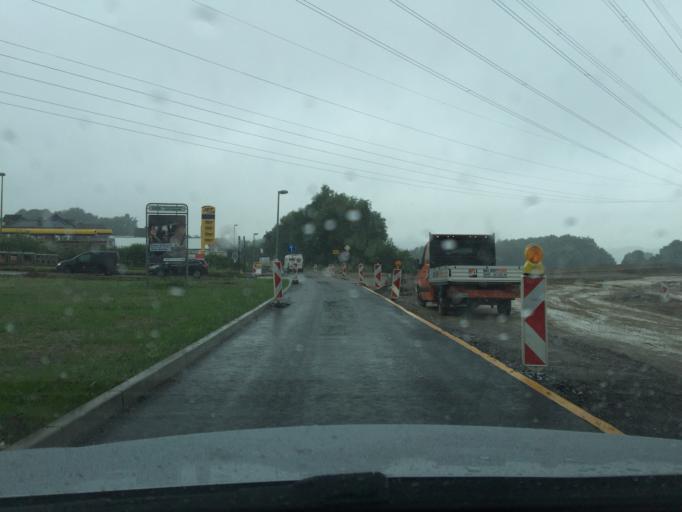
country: DE
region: North Rhine-Westphalia
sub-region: Regierungsbezirk Dusseldorf
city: Velbert
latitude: 51.3292
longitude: 7.0116
